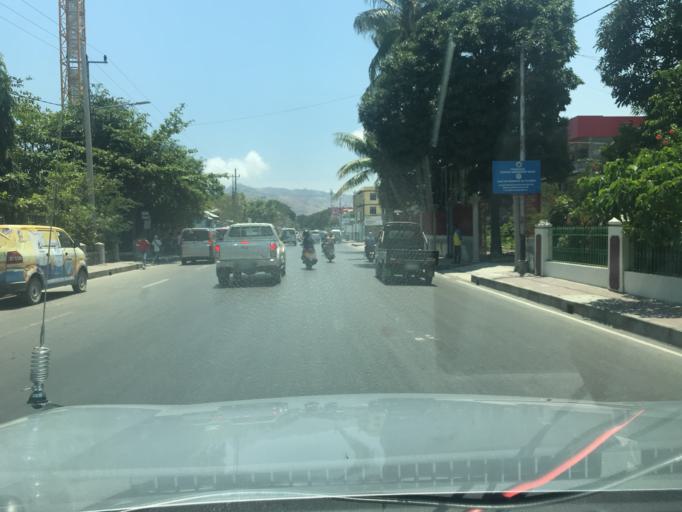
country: TL
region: Dili
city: Dili
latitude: -8.5542
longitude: 125.5696
